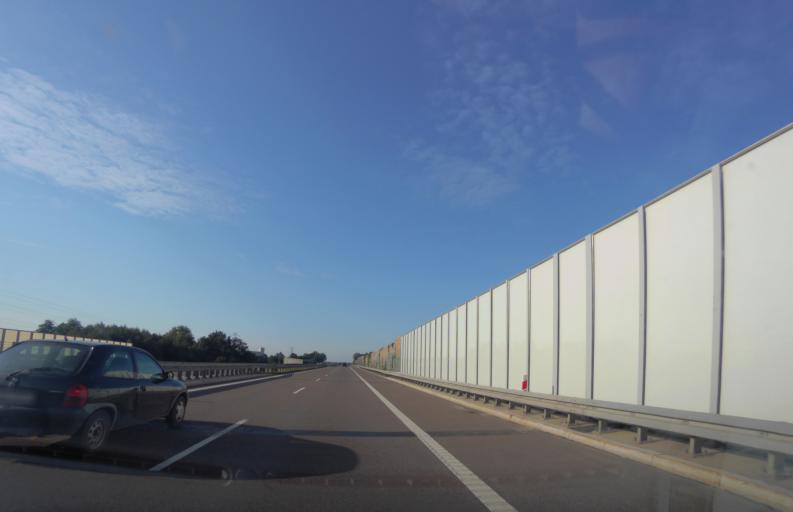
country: PL
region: Subcarpathian Voivodeship
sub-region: Powiat rzeszowski
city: Trzebownisko
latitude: 50.0778
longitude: 22.0593
